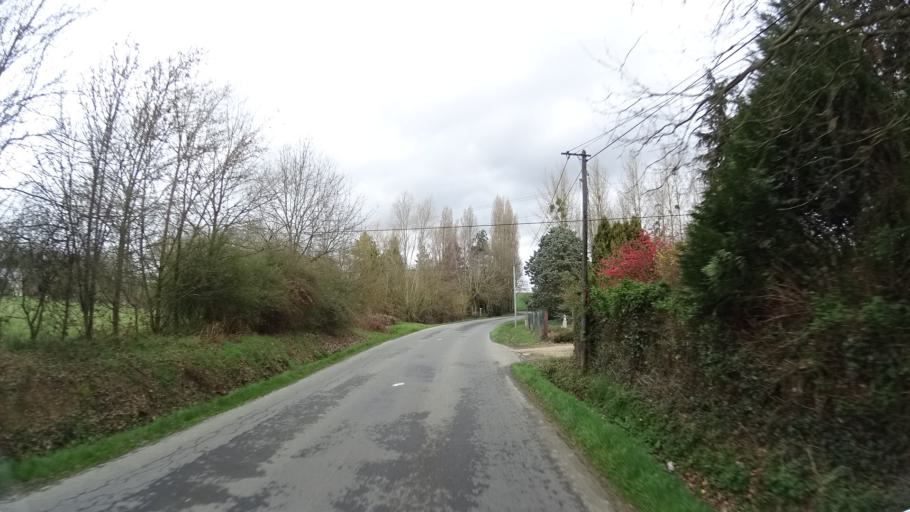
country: FR
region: Brittany
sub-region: Departement d'Ille-et-Vilaine
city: Saint-Gilles
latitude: 48.1698
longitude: -1.8292
